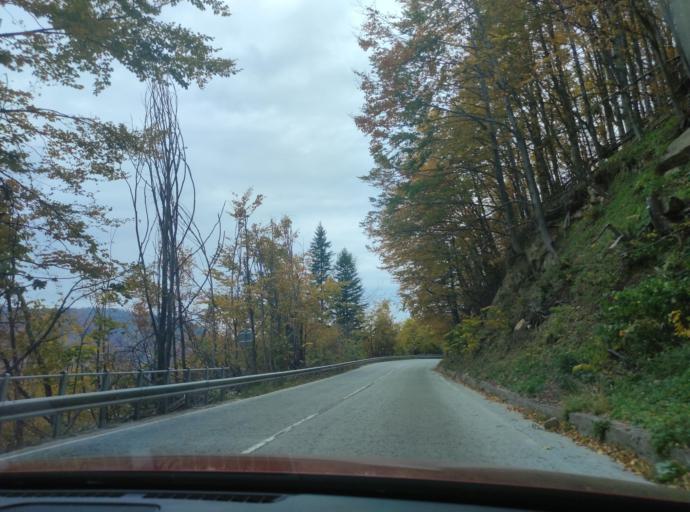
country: BG
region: Montana
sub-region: Obshtina Berkovitsa
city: Berkovitsa
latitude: 43.1458
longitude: 23.1441
